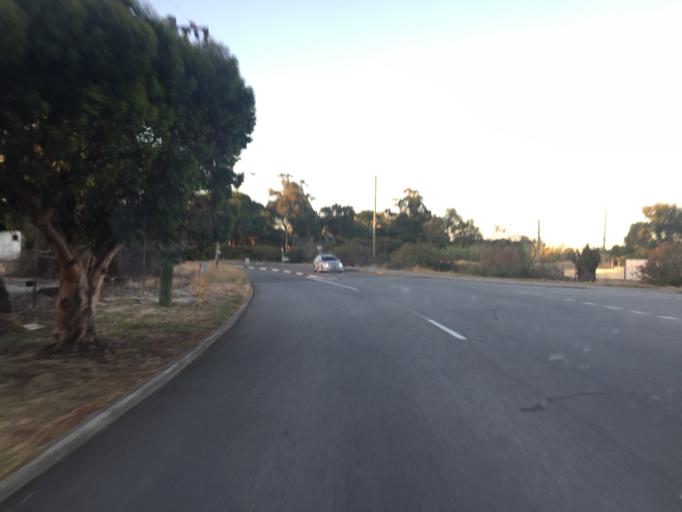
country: AU
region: Western Australia
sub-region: Gosnells
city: Kenwick
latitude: -32.0285
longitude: 115.9823
